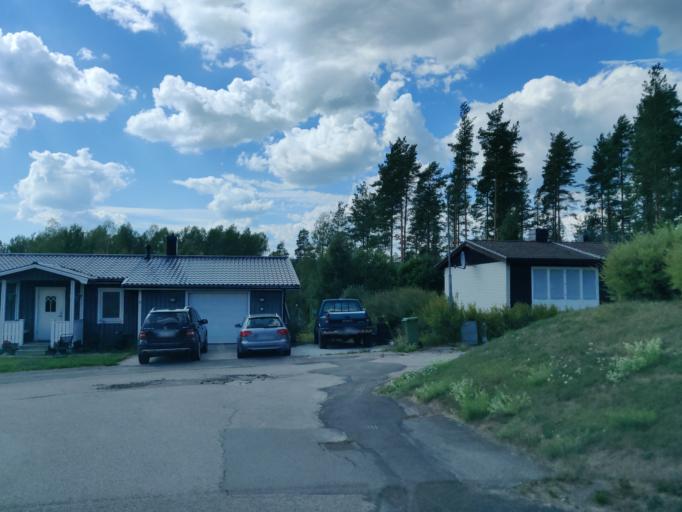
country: SE
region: Vaermland
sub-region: Hagfors Kommun
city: Hagfors
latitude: 59.8845
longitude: 13.7161
